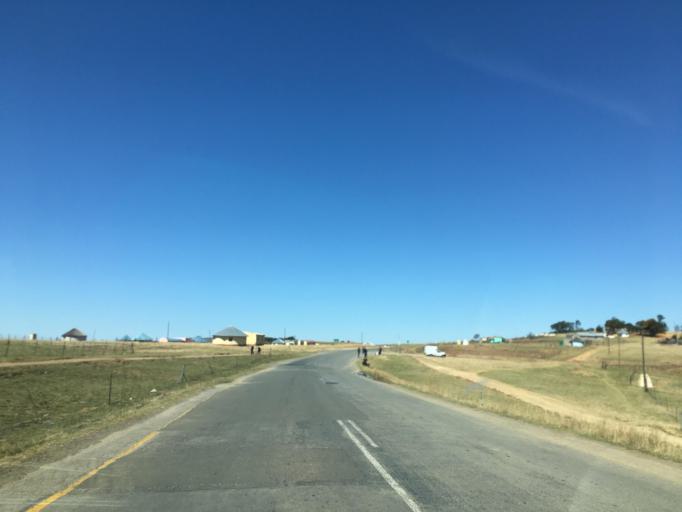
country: ZA
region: Eastern Cape
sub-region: Chris Hani District Municipality
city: Cala
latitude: -31.5560
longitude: 27.8961
